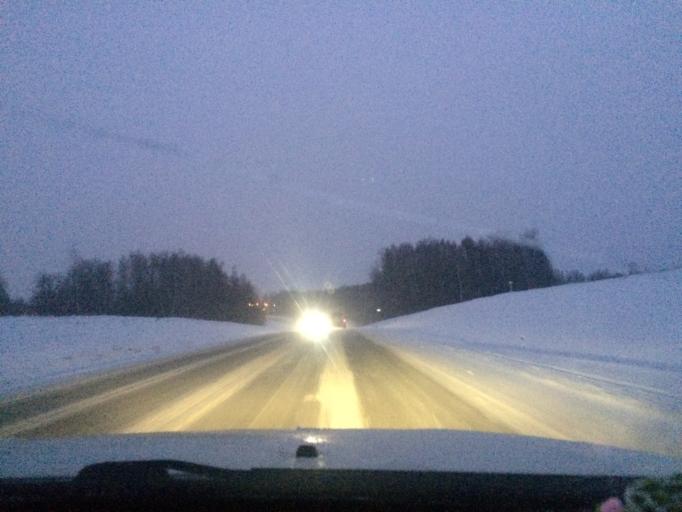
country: RU
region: Tula
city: Kosaya Gora
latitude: 54.1695
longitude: 37.4596
